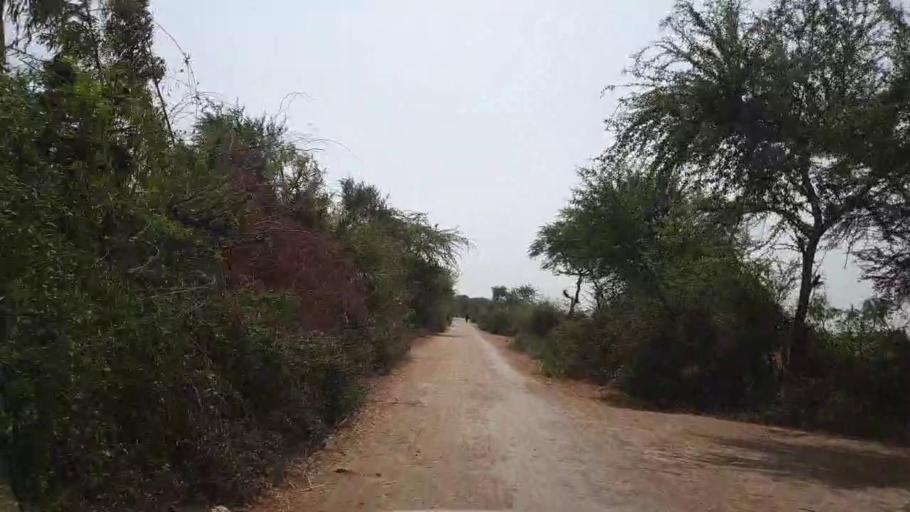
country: PK
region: Sindh
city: Matli
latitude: 25.0311
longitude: 68.7046
